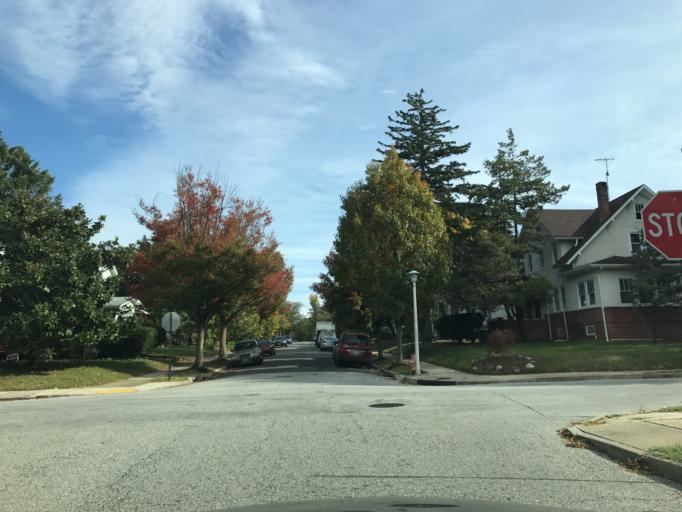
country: US
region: Maryland
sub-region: City of Baltimore
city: Baltimore
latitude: 39.3293
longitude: -76.5924
